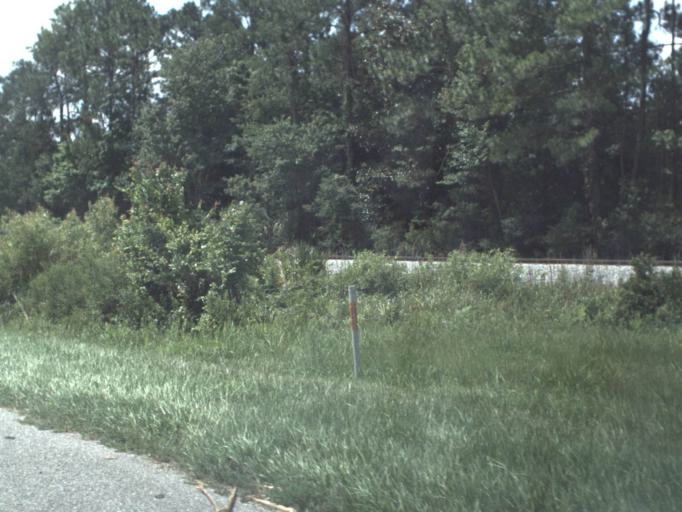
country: US
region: Florida
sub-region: Saint Johns County
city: Palm Valley
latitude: 30.0681
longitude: -81.4423
